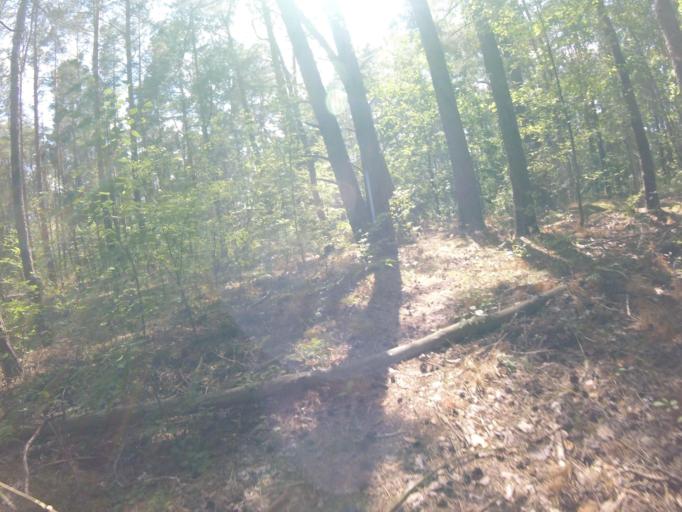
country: DE
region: Brandenburg
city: Wildau
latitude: 52.3277
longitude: 13.6676
